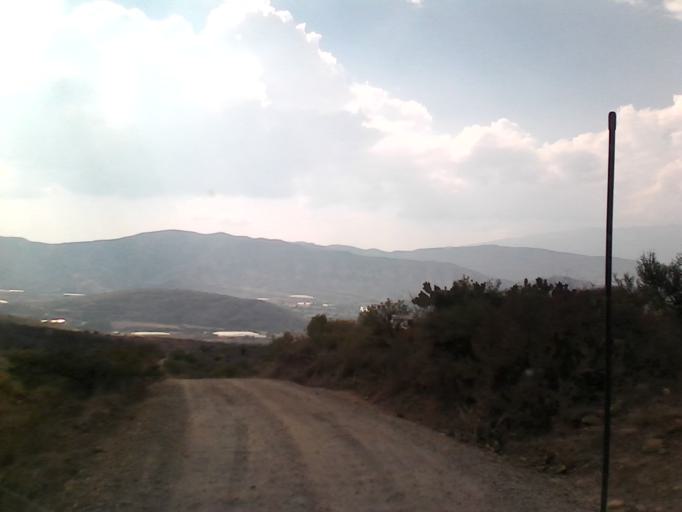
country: CO
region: Boyaca
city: Sachica
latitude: 5.5747
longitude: -73.5216
